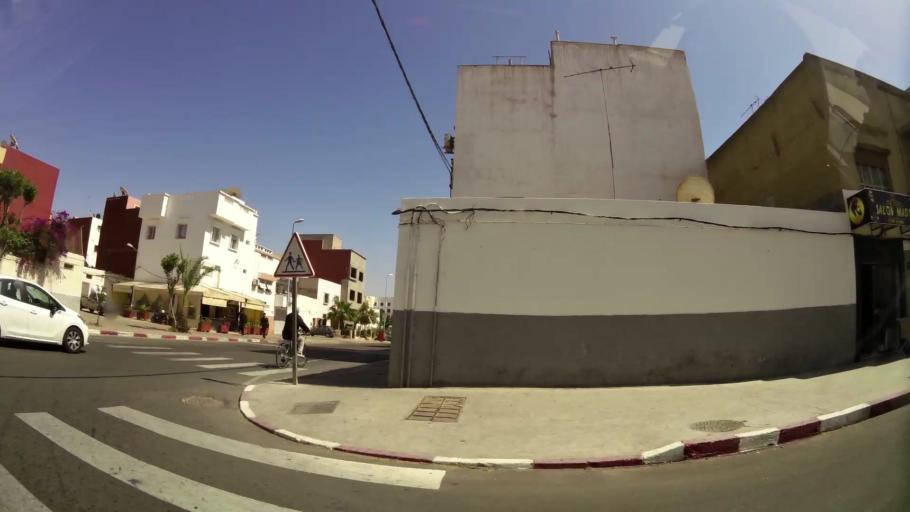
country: MA
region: Souss-Massa-Draa
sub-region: Agadir-Ida-ou-Tnan
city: Agadir
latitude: 30.4124
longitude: -9.5842
